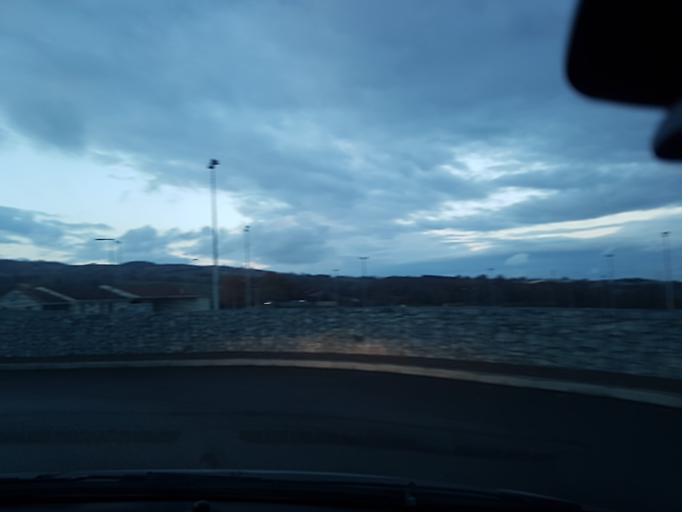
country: FR
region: Rhone-Alpes
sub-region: Departement du Rhone
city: Mornant
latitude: 45.6247
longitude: 4.6735
